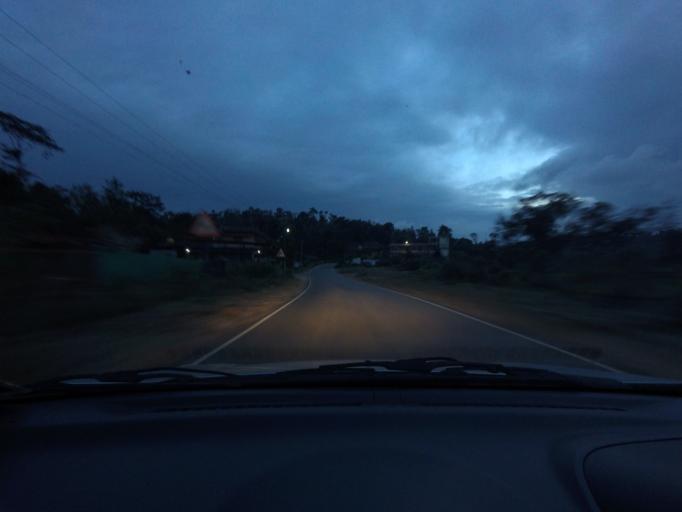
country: IN
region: Karnataka
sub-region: Hassan
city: Sakleshpur
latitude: 13.0025
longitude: 75.6987
